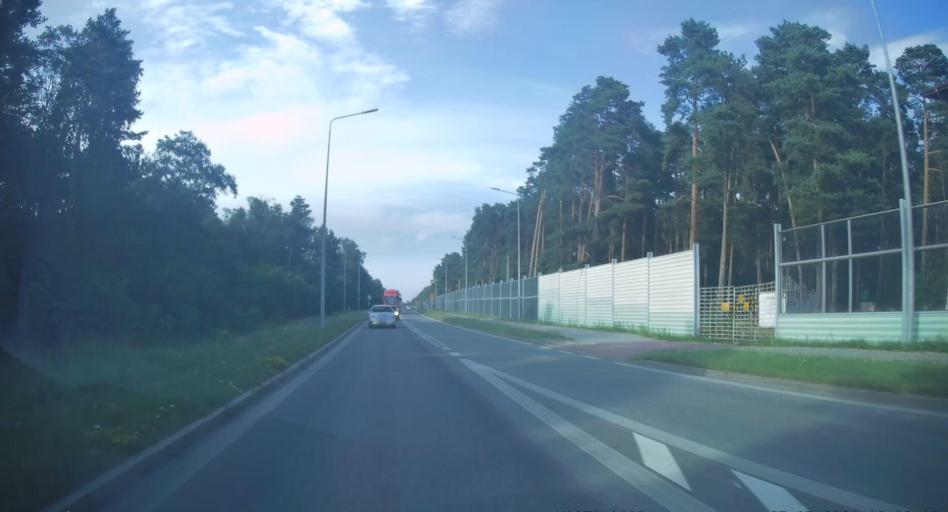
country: PL
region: Swietokrzyskie
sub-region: Powiat konecki
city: Smykow
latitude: 51.1197
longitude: 20.3528
